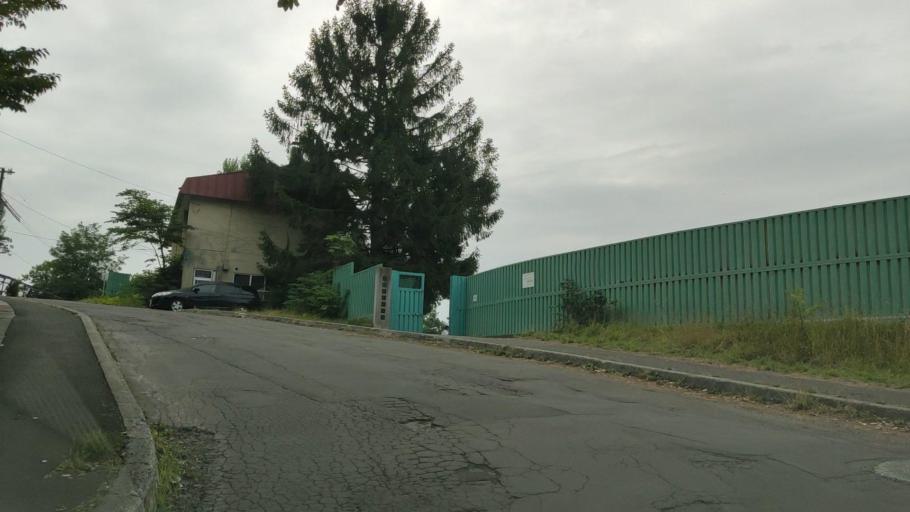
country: JP
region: Hokkaido
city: Otaru
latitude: 43.1872
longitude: 140.9929
